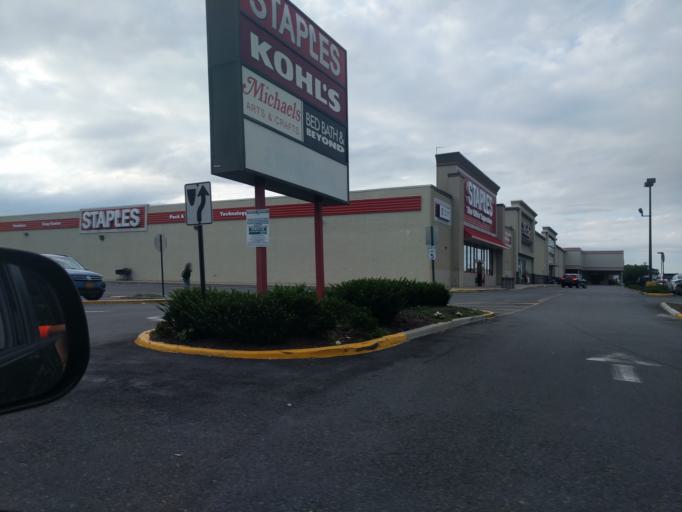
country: US
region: New York
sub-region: Nassau County
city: Barnum Island
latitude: 40.6207
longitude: -73.6423
